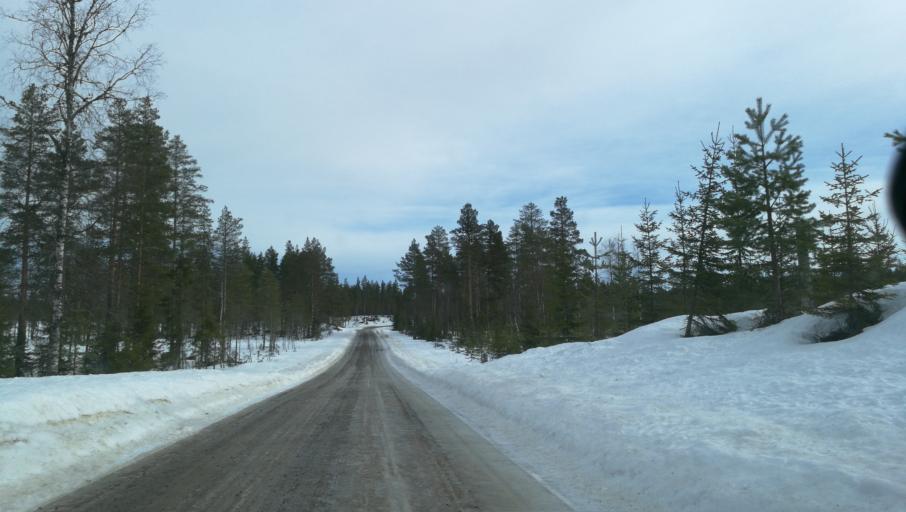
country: SE
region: Vaermland
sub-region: Torsby Kommun
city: Torsby
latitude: 60.6662
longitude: 12.8342
